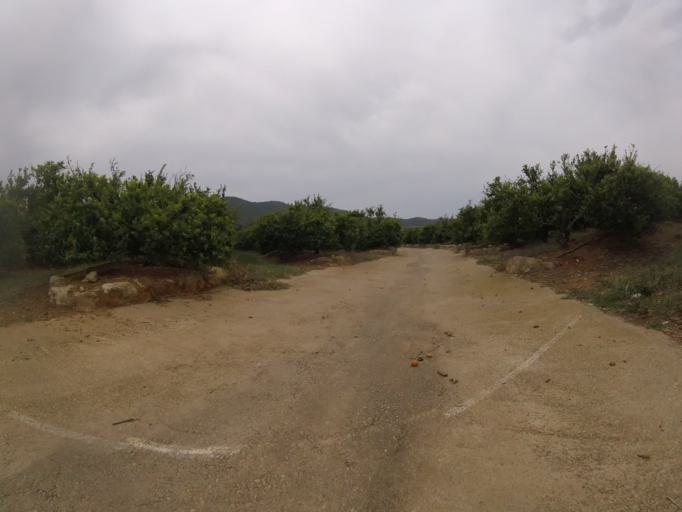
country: ES
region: Valencia
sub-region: Provincia de Castello
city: Alcala de Xivert
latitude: 40.2780
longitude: 0.2527
